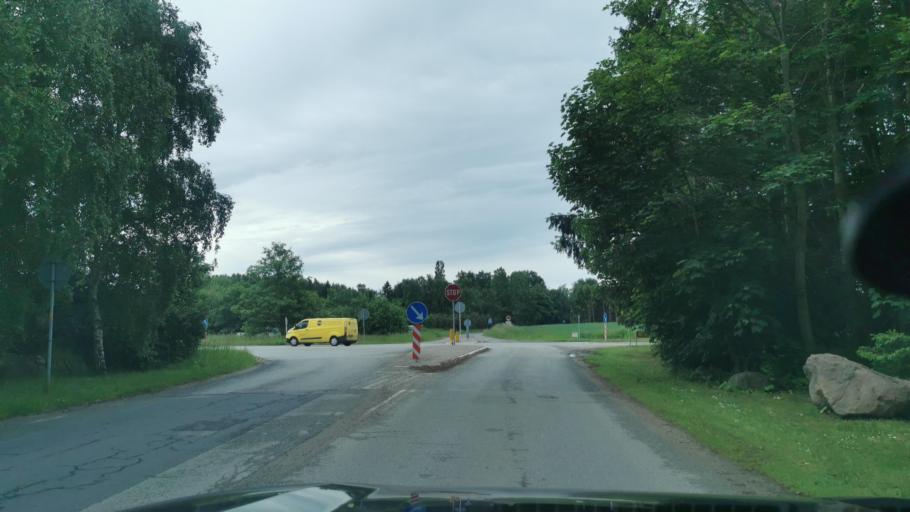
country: DK
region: Capital Region
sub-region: Hillerod Kommune
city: Hillerod
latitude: 55.9361
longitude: 12.2414
